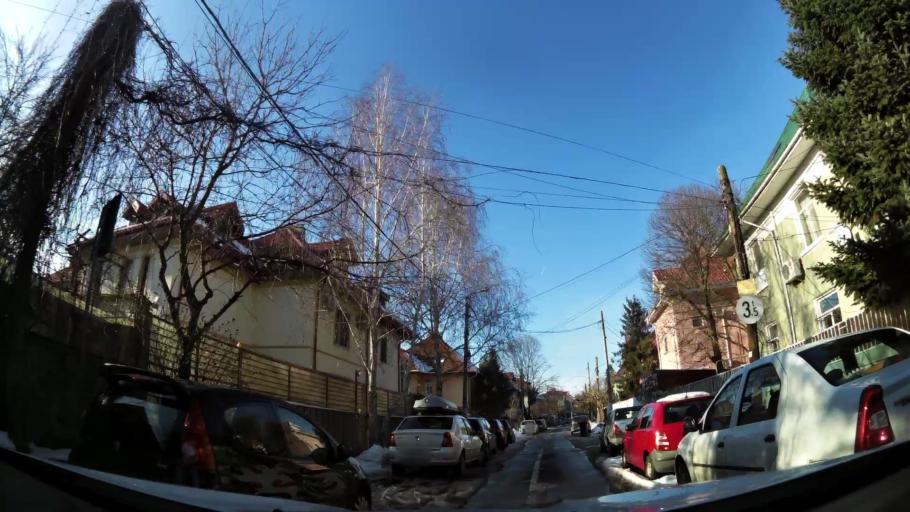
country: RO
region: Bucuresti
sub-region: Municipiul Bucuresti
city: Bucuresti
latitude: 44.4033
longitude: 26.0934
